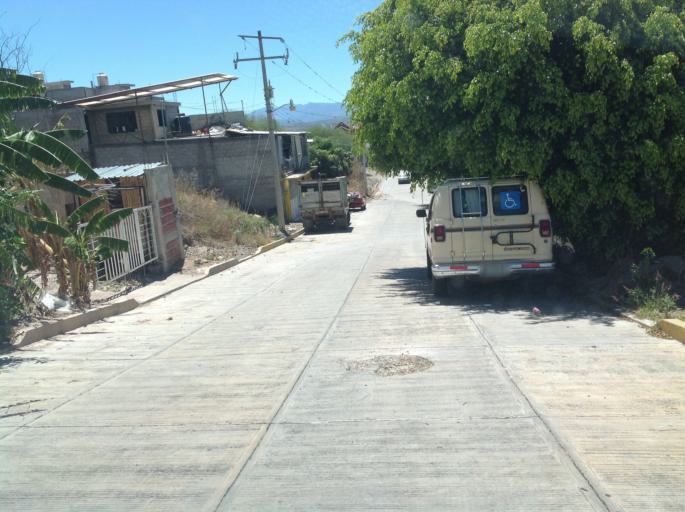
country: MX
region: Oaxaca
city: Ciudad de Huajuapam de Leon
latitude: 17.8175
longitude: -97.7744
